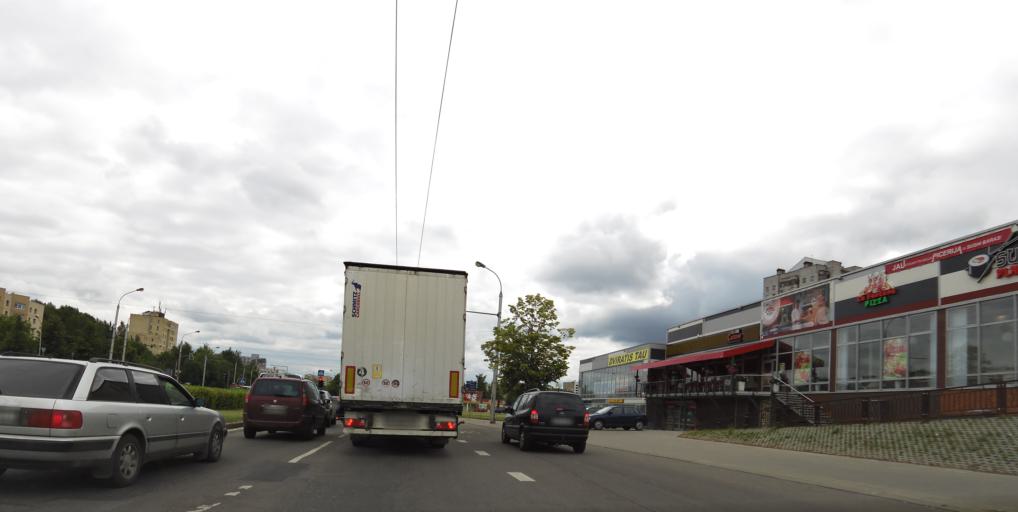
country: LT
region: Vilnius County
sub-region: Vilnius
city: Fabijoniskes
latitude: 54.7270
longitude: 25.2335
